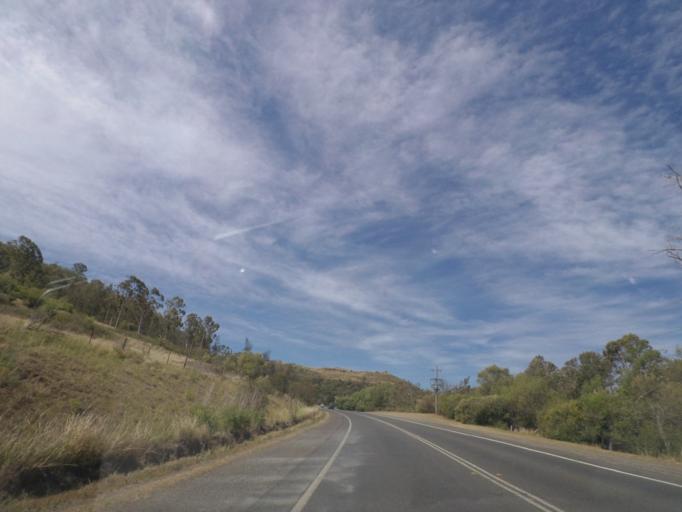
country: AU
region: New South Wales
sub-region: Wollondilly
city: Picton
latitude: -34.1625
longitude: 150.6394
